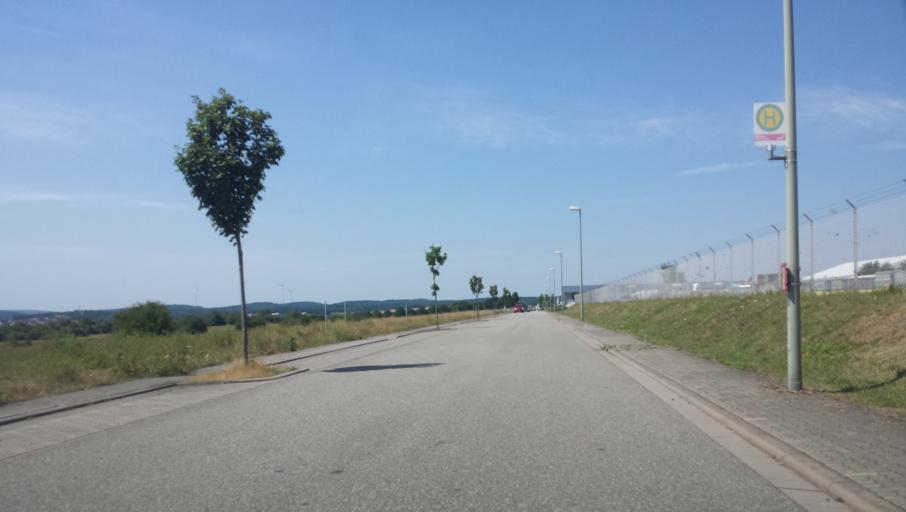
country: DE
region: Rheinland-Pfalz
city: Sembach
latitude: 49.5097
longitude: 7.8695
